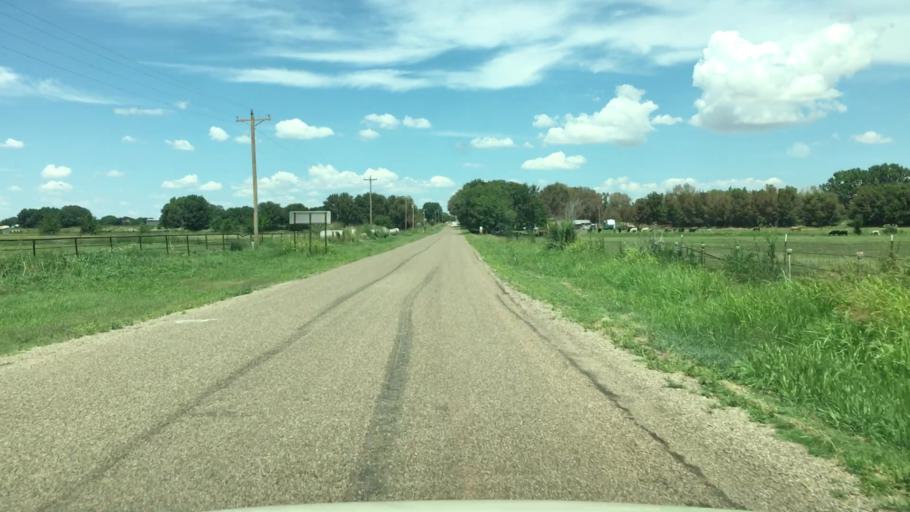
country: US
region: New Mexico
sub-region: De Baca County
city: Fort Sumner
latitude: 34.4344
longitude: -104.1935
